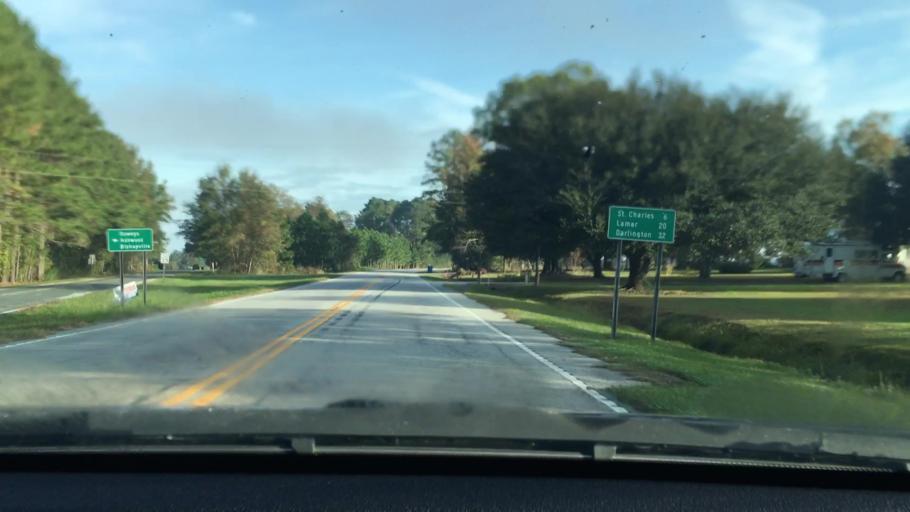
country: US
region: South Carolina
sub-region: Sumter County
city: East Sumter
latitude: 34.0059
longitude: -80.2873
